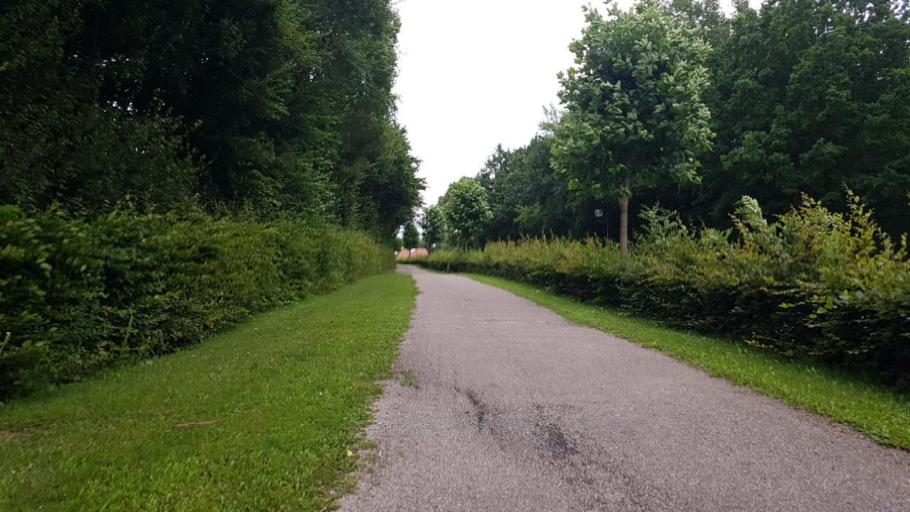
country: FR
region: Picardie
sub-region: Departement de l'Aisne
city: Hirson
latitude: 49.9119
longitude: 4.0606
